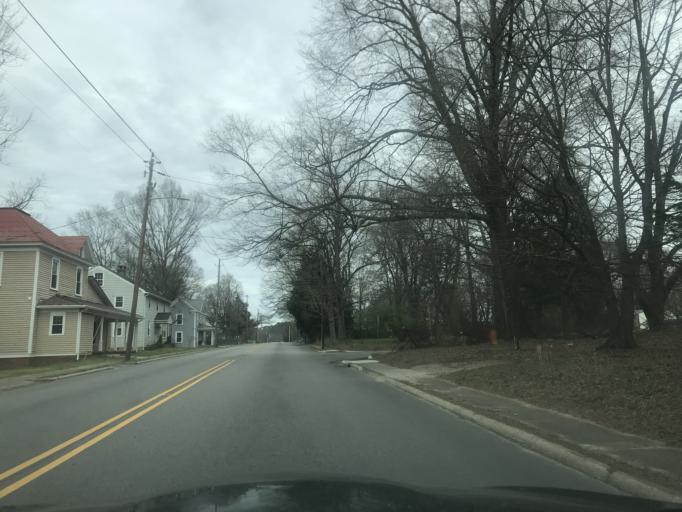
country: US
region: North Carolina
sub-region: Franklin County
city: Franklinton
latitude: 36.1022
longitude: -78.4516
